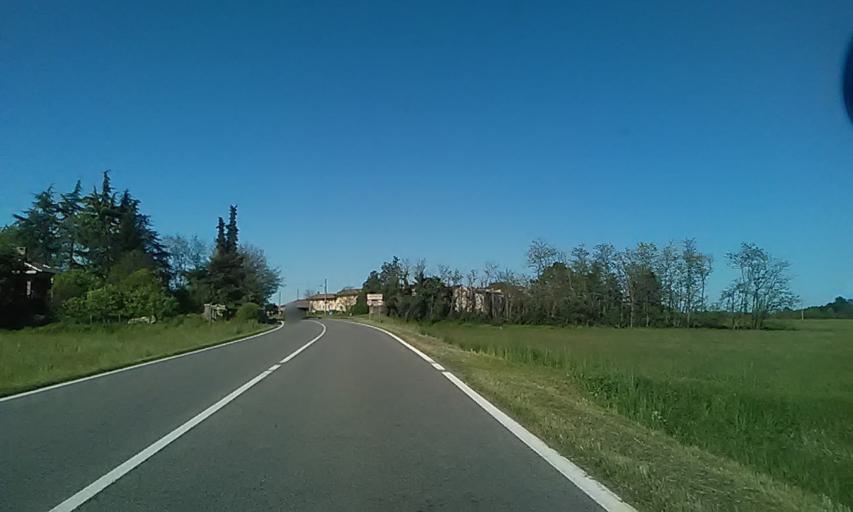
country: IT
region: Piedmont
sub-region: Provincia di Novara
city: Momo
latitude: 45.5830
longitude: 8.5795
